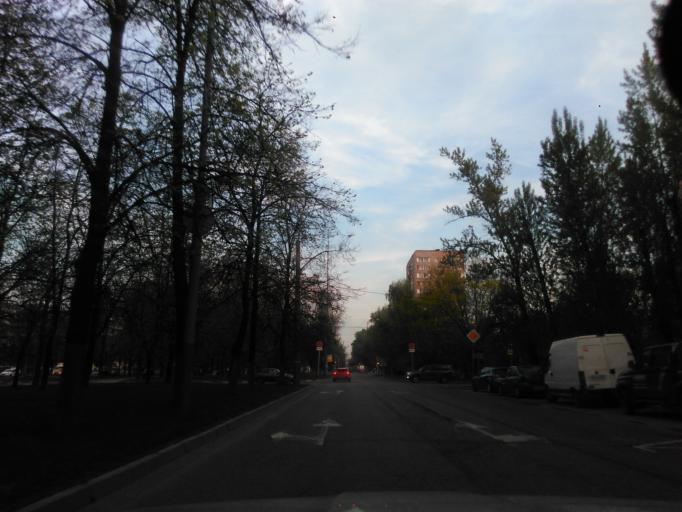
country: RU
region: Moscow
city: Novyye Kuz'minki
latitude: 55.7020
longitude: 37.7492
